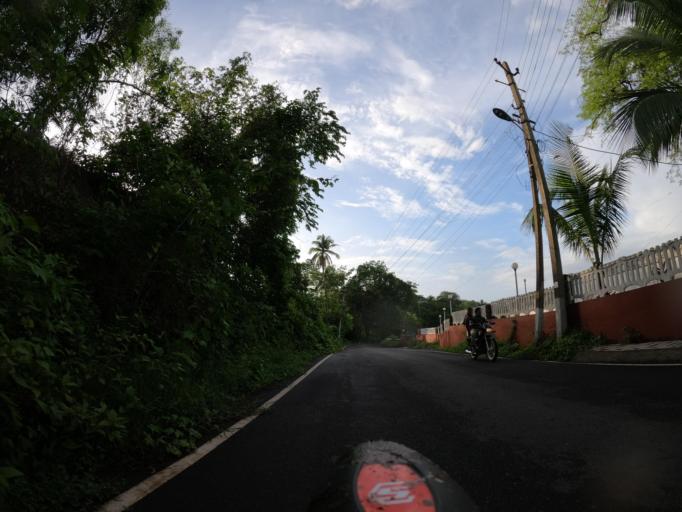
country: IN
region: Goa
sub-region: North Goa
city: Panaji
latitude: 15.5090
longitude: 73.8427
